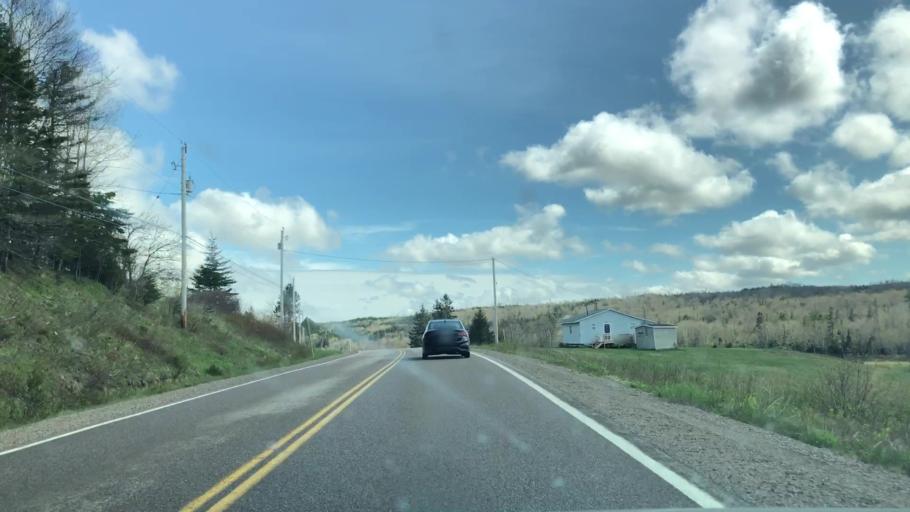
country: CA
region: Nova Scotia
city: Antigonish
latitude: 45.1986
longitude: -62.0025
